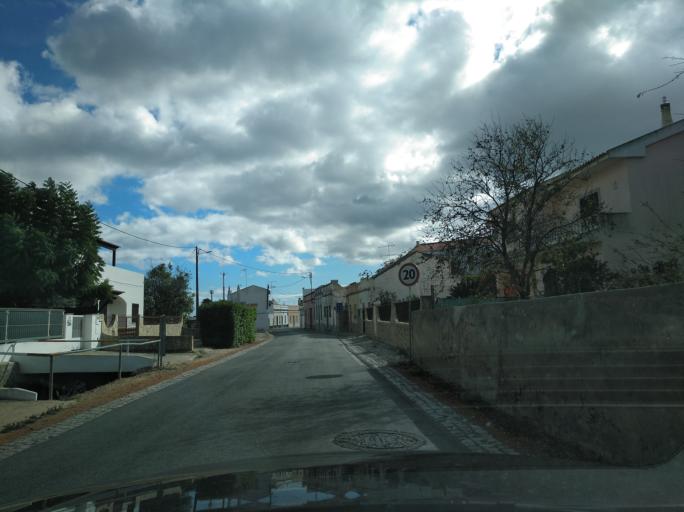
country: PT
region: Faro
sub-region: Tavira
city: Luz
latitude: 37.0944
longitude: -7.7044
